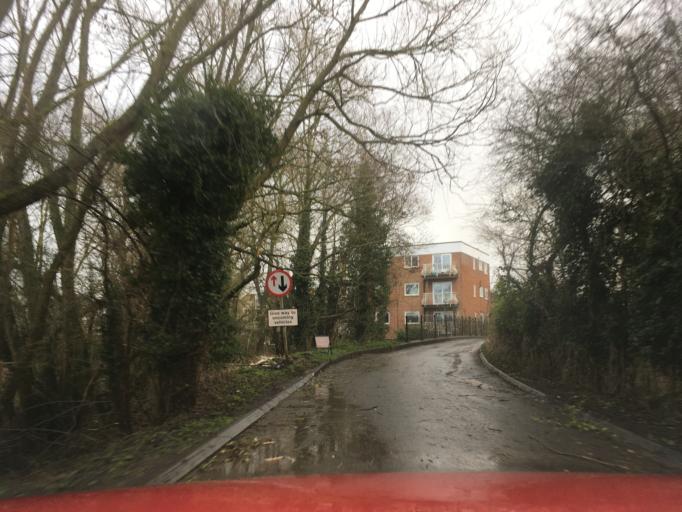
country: GB
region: England
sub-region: Oxfordshire
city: Oxford
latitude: 51.7544
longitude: -1.2800
